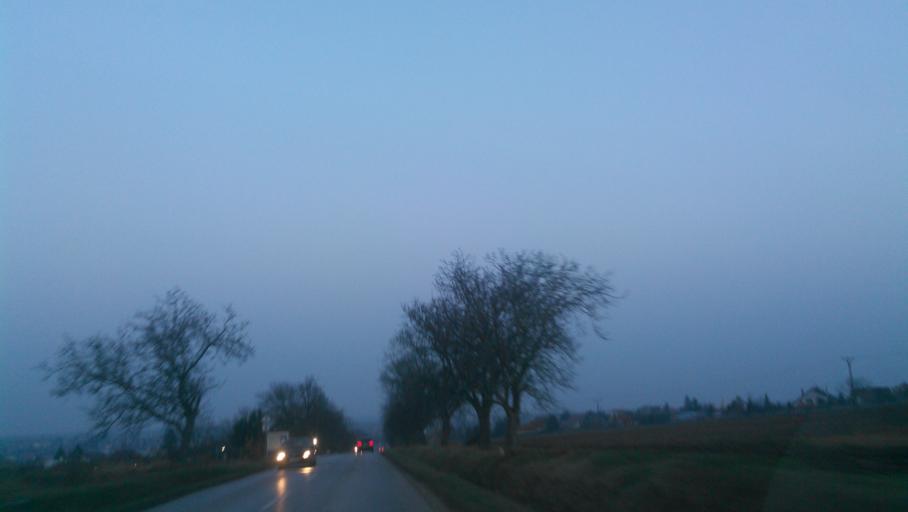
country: SK
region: Bratislavsky
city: Modra
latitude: 48.2979
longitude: 17.3317
